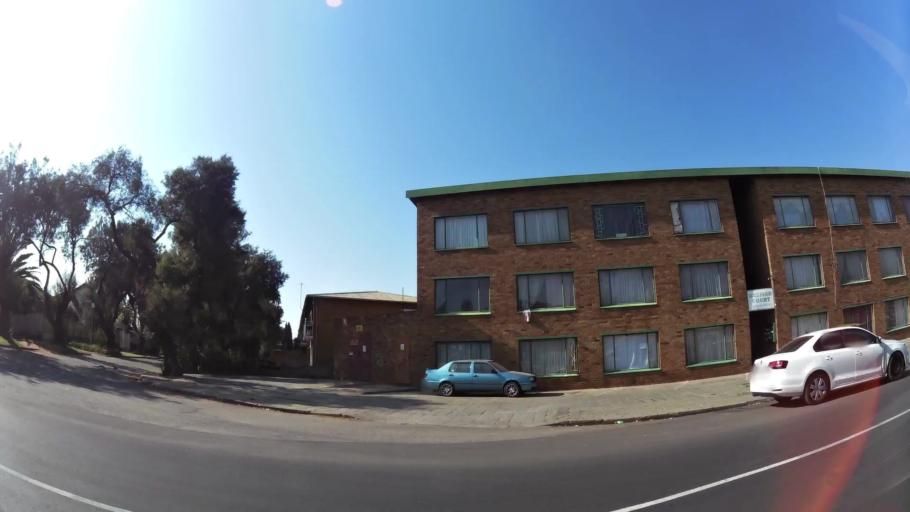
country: ZA
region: Gauteng
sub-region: Ekurhuleni Metropolitan Municipality
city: Boksburg
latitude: -26.2267
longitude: 28.2609
